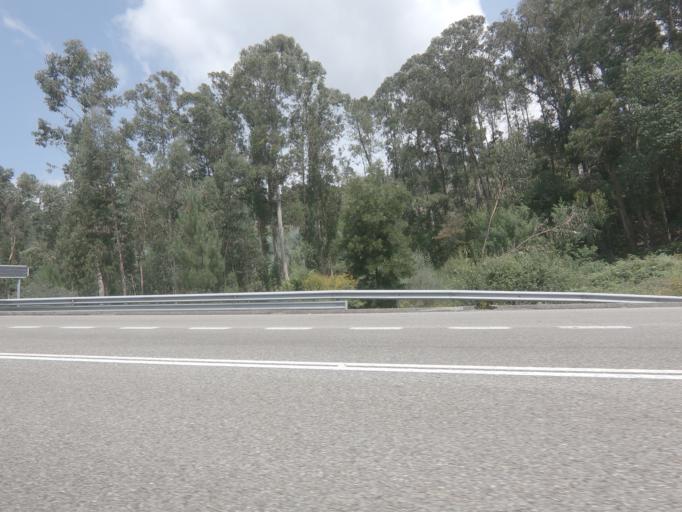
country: ES
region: Galicia
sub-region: Provincia de Pontevedra
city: Tomino
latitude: 42.0450
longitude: -8.7282
